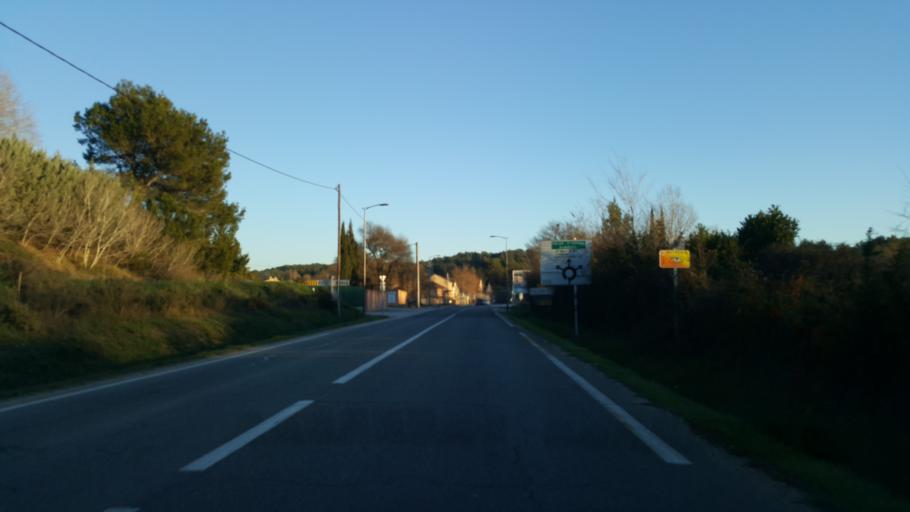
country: FR
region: Provence-Alpes-Cote d'Azur
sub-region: Departement des Bouches-du-Rhone
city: Le Tholonet
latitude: 43.5027
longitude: 5.5131
